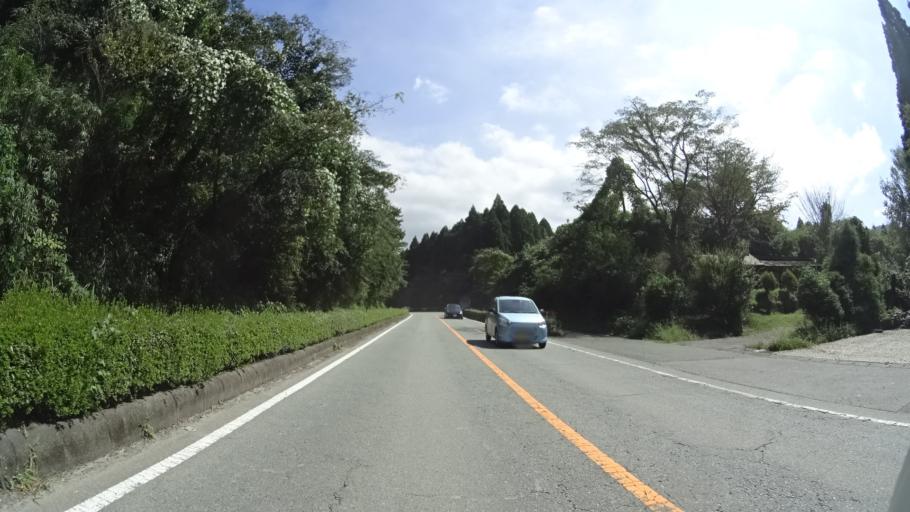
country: JP
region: Kumamoto
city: Aso
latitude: 32.8584
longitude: 131.0068
